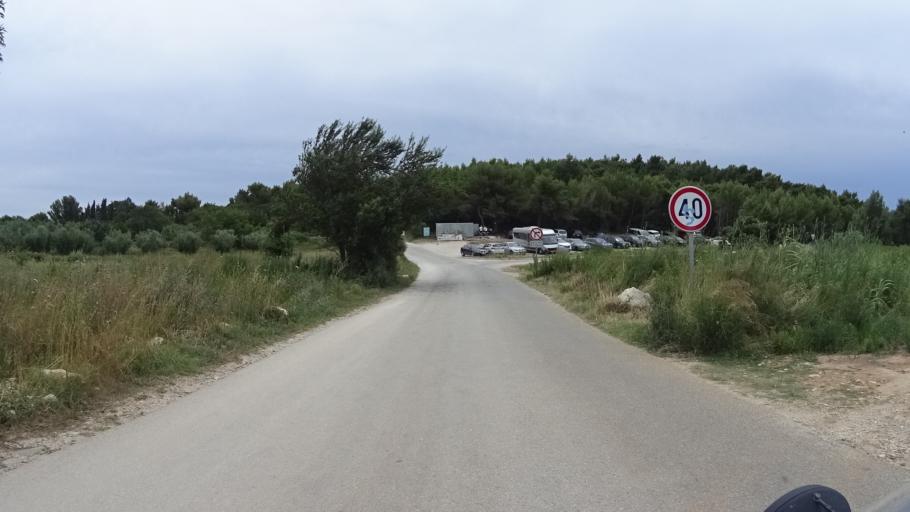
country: HR
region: Istarska
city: Medulin
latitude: 44.7983
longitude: 13.9061
